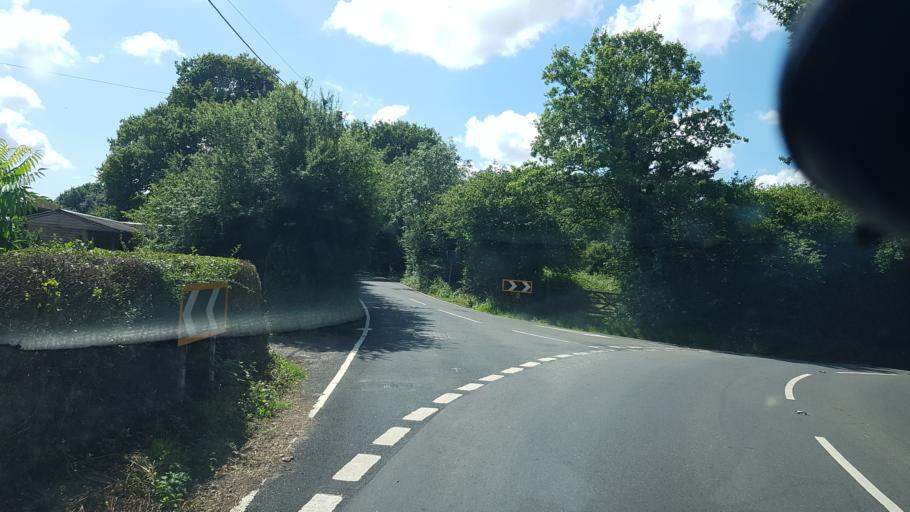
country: GB
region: England
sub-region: Kent
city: Edenbridge
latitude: 51.2272
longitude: 0.1299
